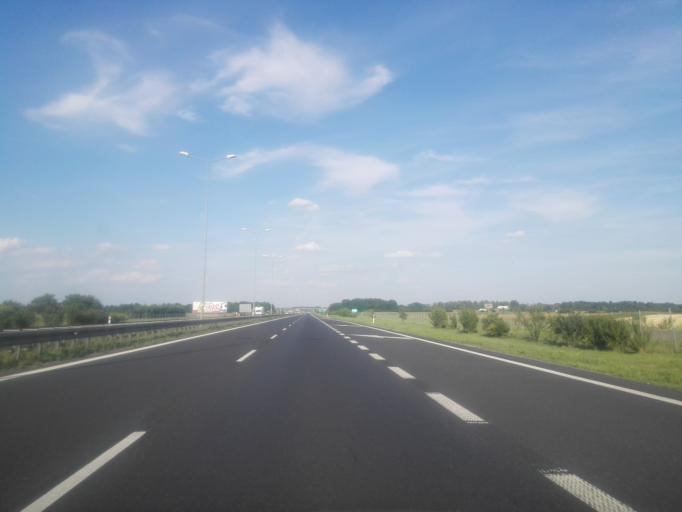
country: PL
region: Lower Silesian Voivodeship
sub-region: Powiat olesnicki
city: Olesnica
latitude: 51.2306
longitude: 17.3772
